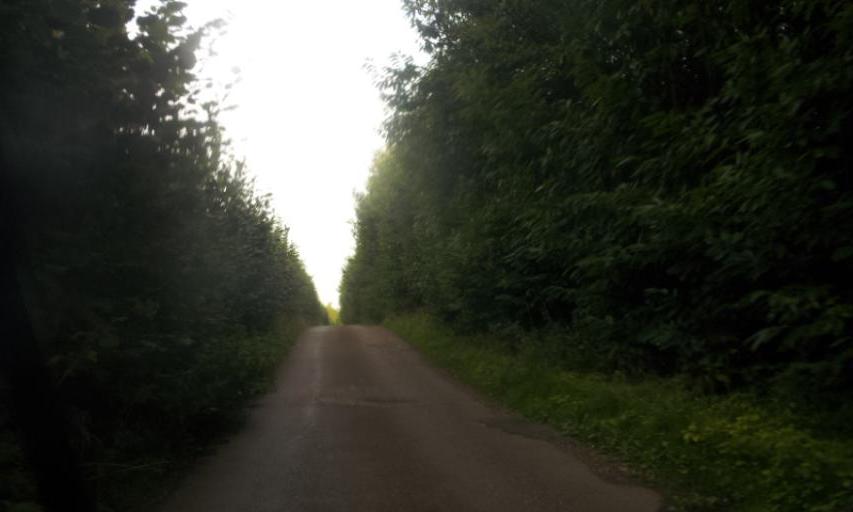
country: GB
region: England
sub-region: Kent
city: Wateringbury
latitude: 51.2670
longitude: 0.4345
